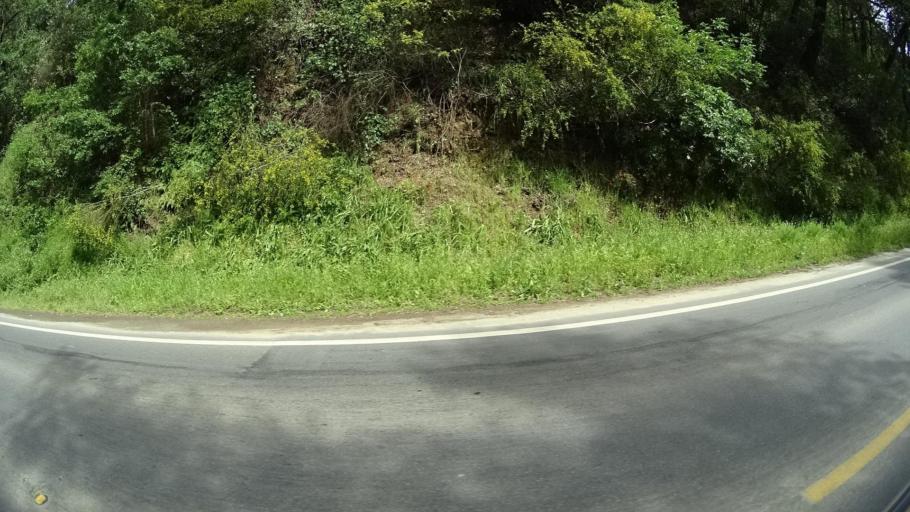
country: US
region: California
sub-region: Humboldt County
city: Redway
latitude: 40.1156
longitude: -123.8091
